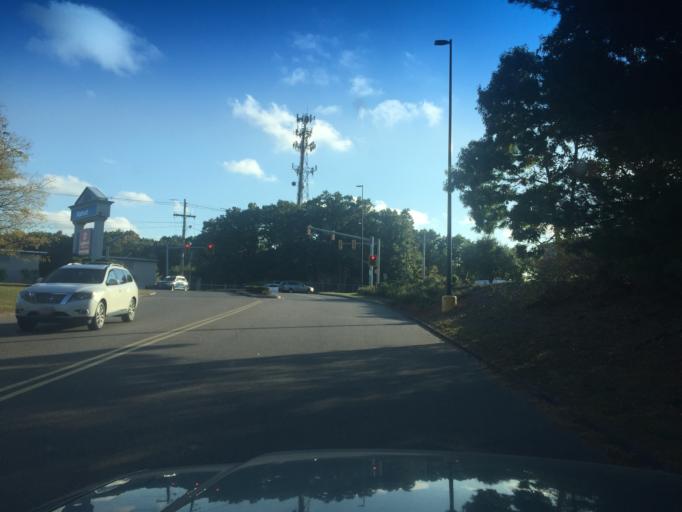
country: US
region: Massachusetts
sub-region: Norfolk County
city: Walpole
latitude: 42.1410
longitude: -71.2166
